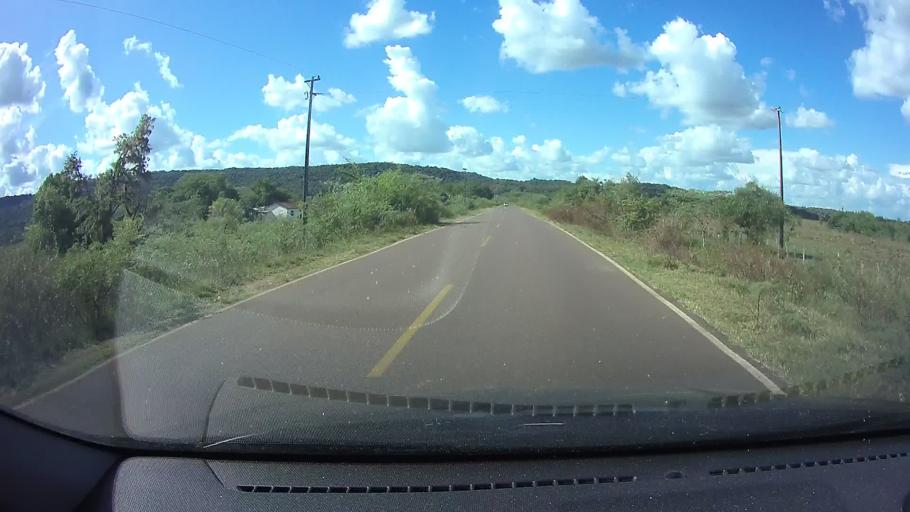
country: PY
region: Paraguari
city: Sapucai
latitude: -25.6800
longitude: -56.8626
